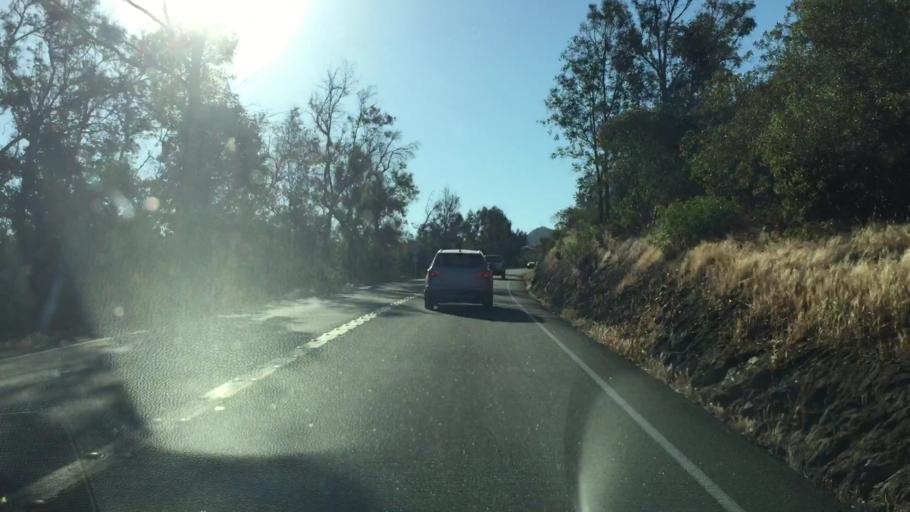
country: US
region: California
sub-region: San Diego County
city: Poway
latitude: 32.9784
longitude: -116.9850
